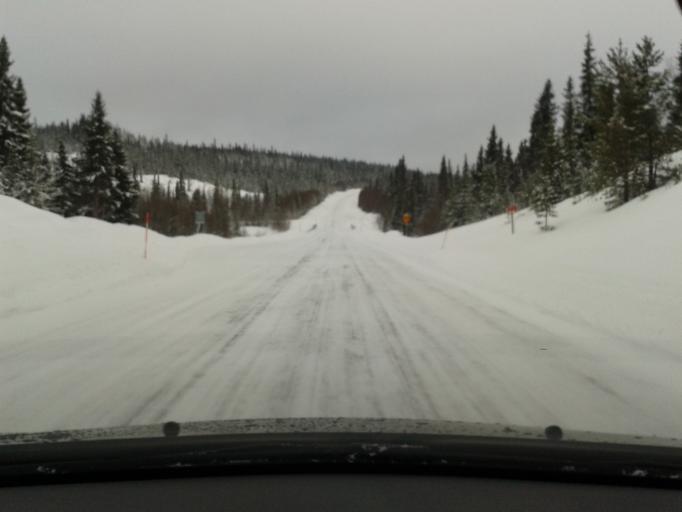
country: SE
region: Vaesterbotten
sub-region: Vilhelmina Kommun
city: Sjoberg
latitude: 65.0308
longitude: 15.8752
